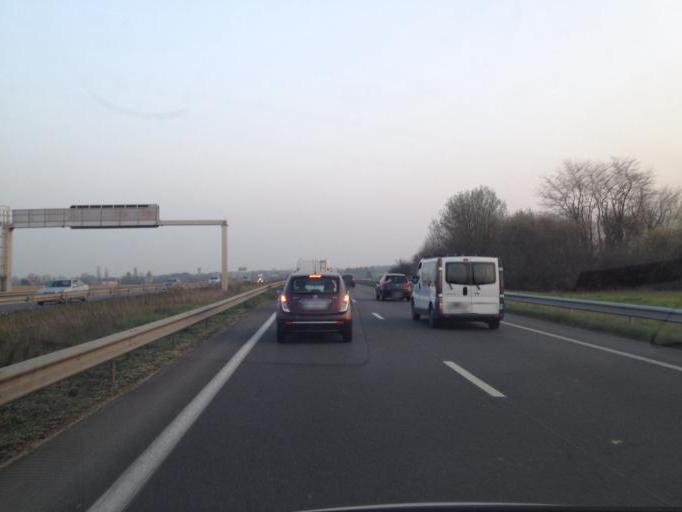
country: FR
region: Ile-de-France
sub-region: Departement de l'Essonne
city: Saclay
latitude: 48.7202
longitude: 2.1692
